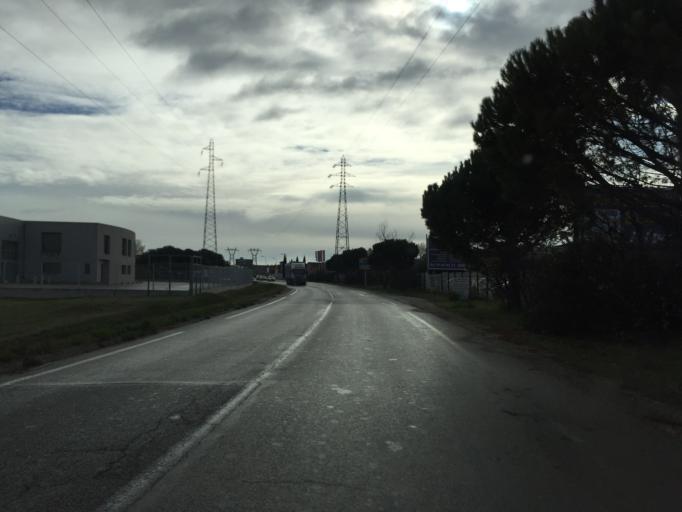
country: FR
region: Provence-Alpes-Cote d'Azur
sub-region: Departement du Vaucluse
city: Sorgues
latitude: 44.0165
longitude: 4.8835
